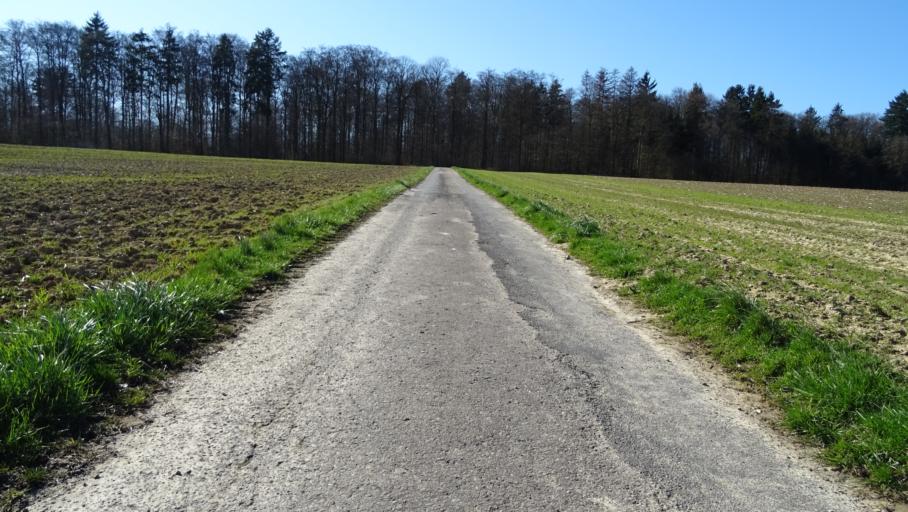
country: DE
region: Baden-Wuerttemberg
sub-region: Karlsruhe Region
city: Seckach
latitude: 49.4385
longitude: 9.3051
